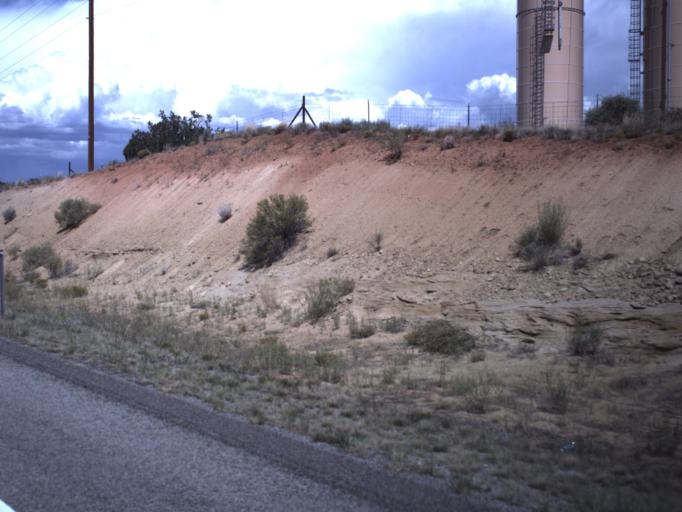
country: US
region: Utah
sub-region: San Juan County
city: Blanding
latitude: 37.4815
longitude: -109.4706
